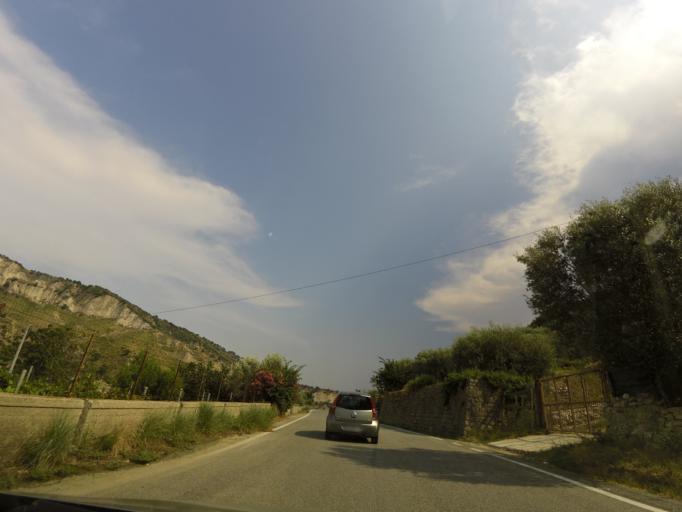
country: IT
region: Calabria
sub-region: Provincia di Reggio Calabria
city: Stilo
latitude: 38.4811
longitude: 16.4779
